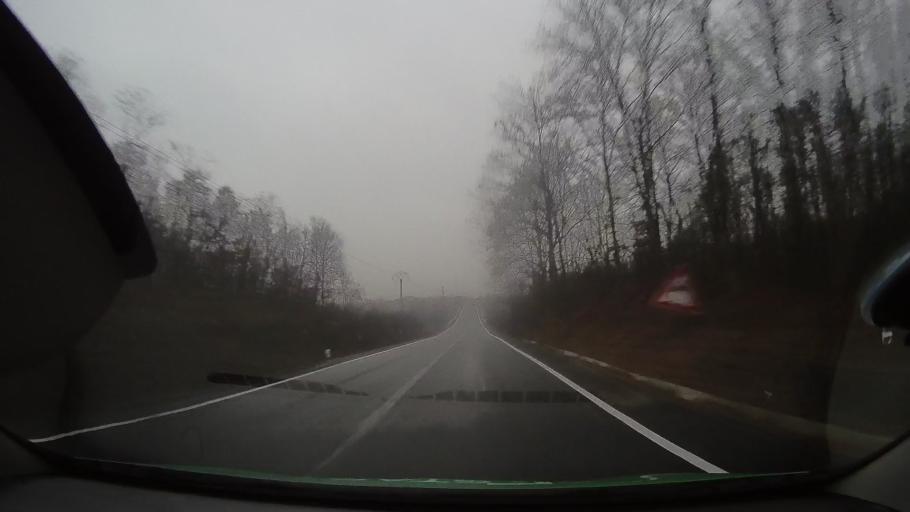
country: RO
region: Bihor
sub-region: Comuna Olcea
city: Olcea
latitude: 46.6954
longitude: 21.9650
